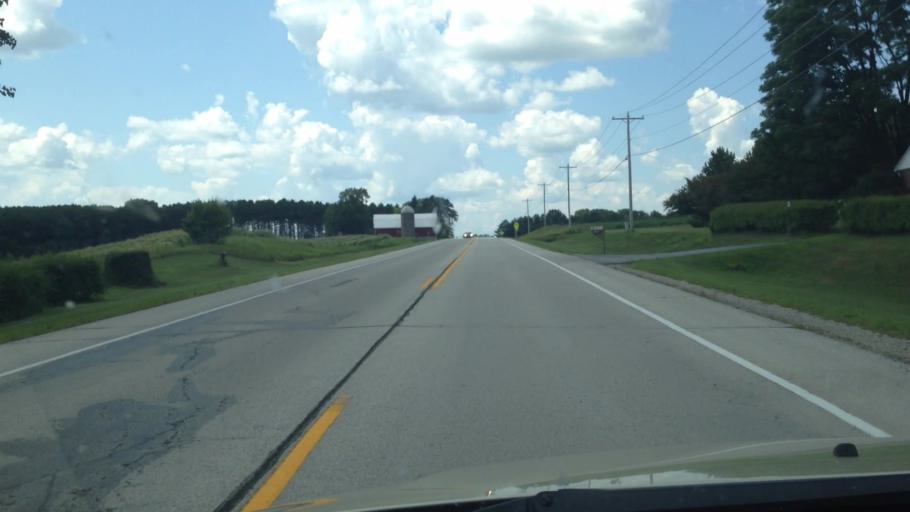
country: US
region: Wisconsin
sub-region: Brown County
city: Suamico
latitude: 44.6354
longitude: -88.0593
